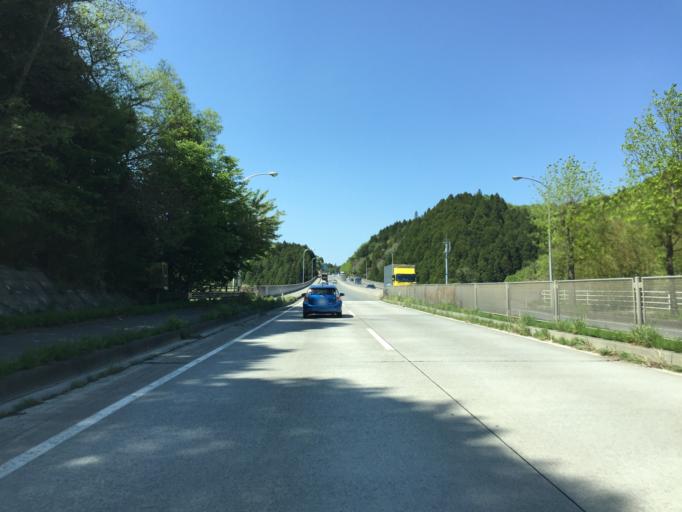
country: JP
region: Fukushima
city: Iwaki
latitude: 37.0112
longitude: 140.8964
